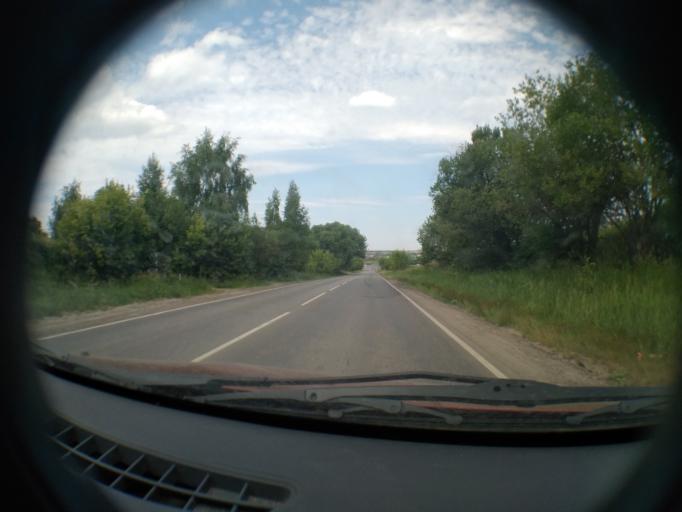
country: RU
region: Moskovskaya
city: Ostrovtsy
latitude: 55.5280
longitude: 38.0011
